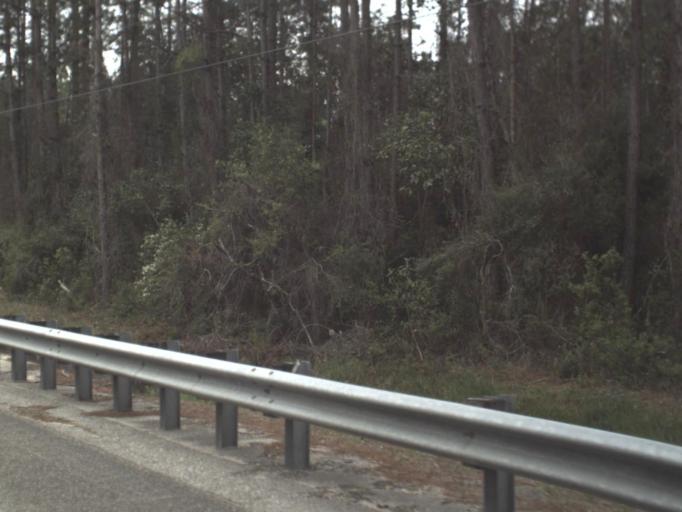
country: US
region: Florida
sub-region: Gulf County
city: Port Saint Joe
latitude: 29.8443
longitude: -85.2648
